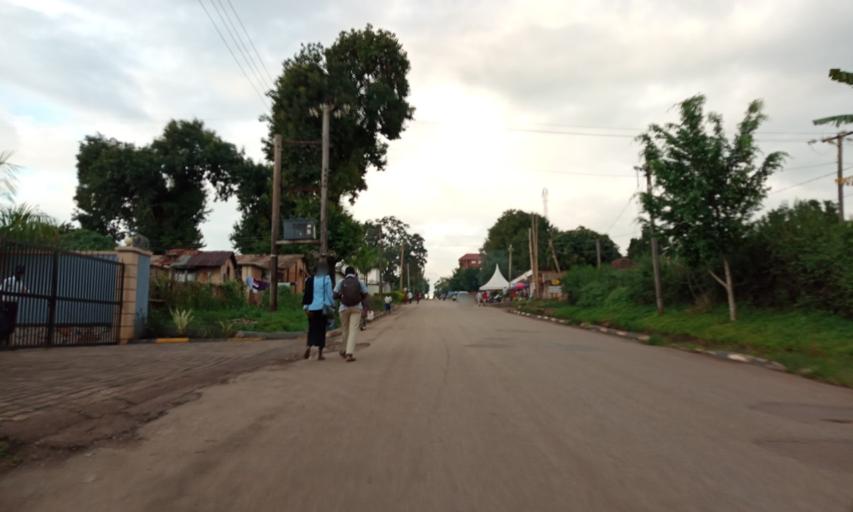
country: UG
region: Eastern Region
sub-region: Mbale District
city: Mbale
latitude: 1.0685
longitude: 34.1802
